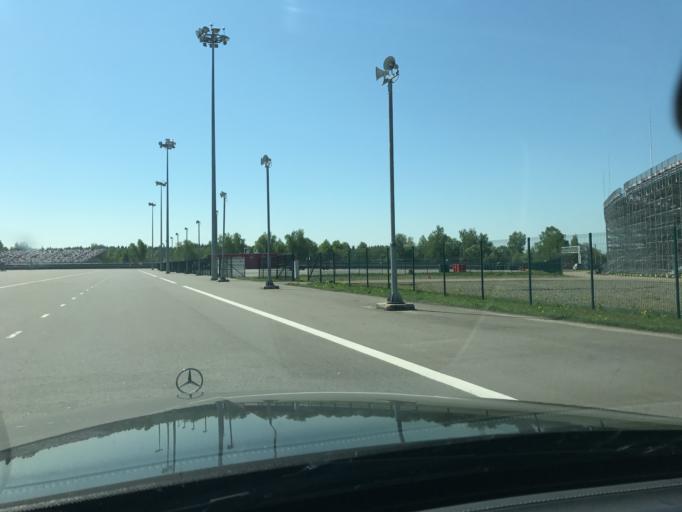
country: RU
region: Moskovskaya
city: Sychevo
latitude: 55.9963
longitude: 36.2686
